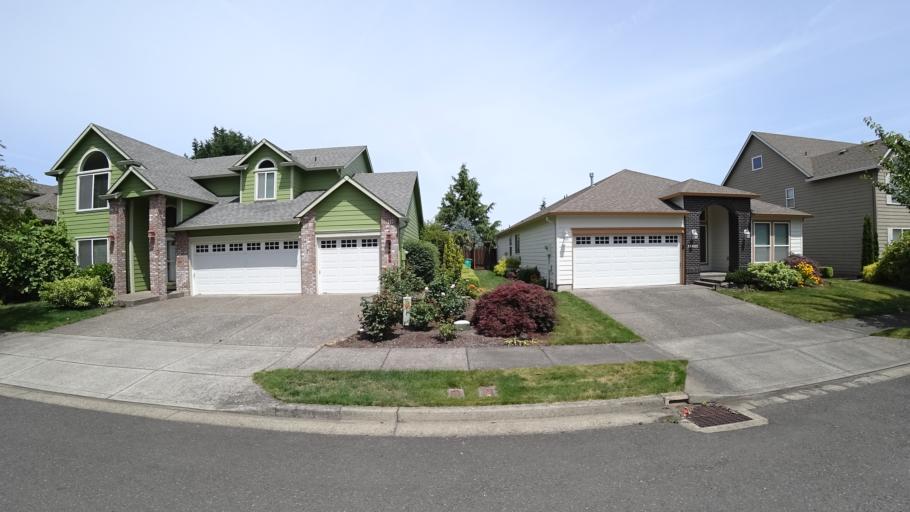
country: US
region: Oregon
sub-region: Multnomah County
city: Fairview
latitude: 45.5471
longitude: -122.4933
